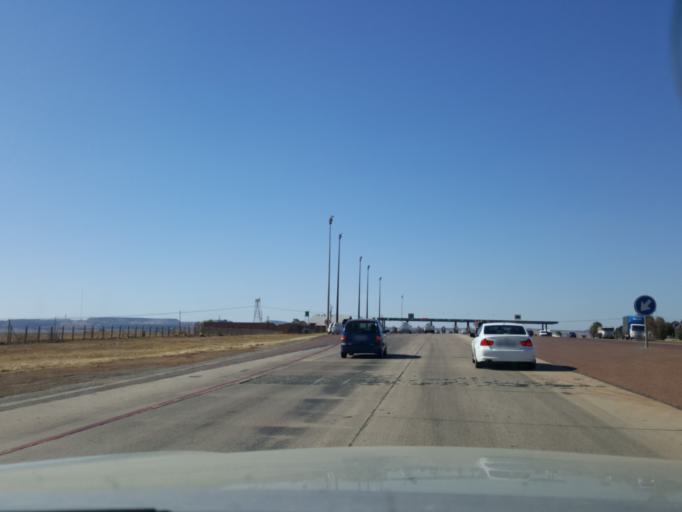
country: ZA
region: Mpumalanga
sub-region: Nkangala District Municipality
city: Witbank
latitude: -25.8676
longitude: 29.3610
